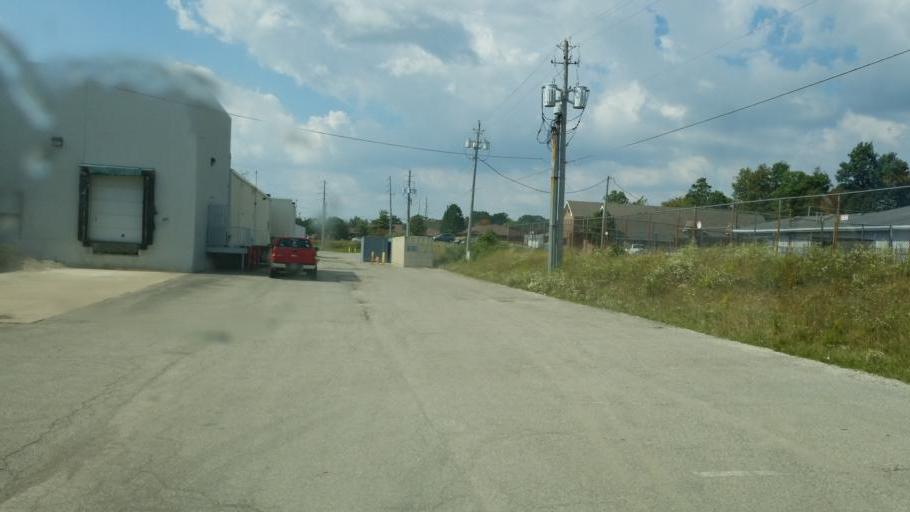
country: US
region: Ohio
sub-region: Richland County
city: Ontario
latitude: 40.7746
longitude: -82.5934
